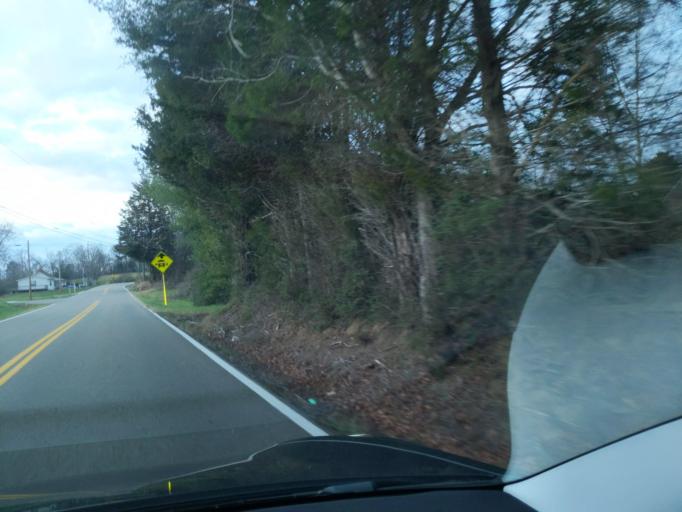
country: US
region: Tennessee
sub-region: Jefferson County
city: Dandridge
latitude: 36.0276
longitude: -83.4099
